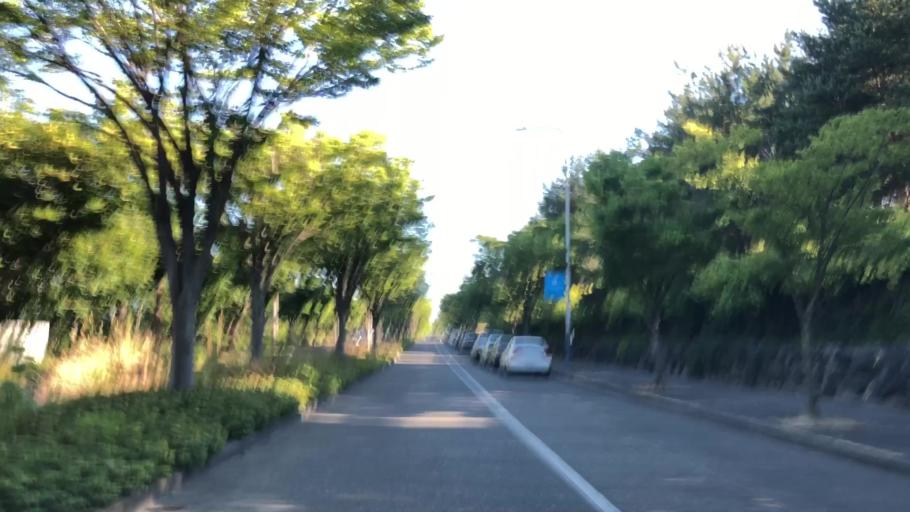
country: US
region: Washington
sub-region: King County
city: White Center
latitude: 47.5467
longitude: -122.3549
